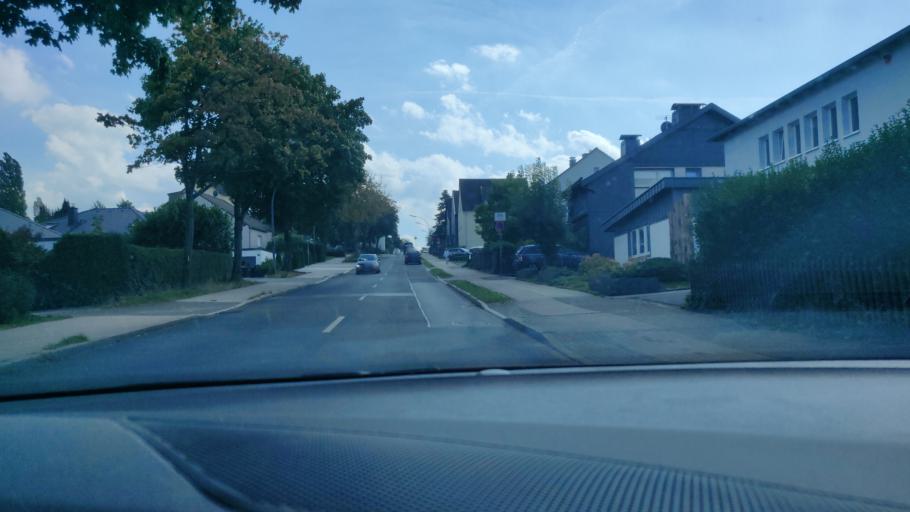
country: DE
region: North Rhine-Westphalia
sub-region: Regierungsbezirk Dusseldorf
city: Velbert
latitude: 51.3497
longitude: 7.0367
